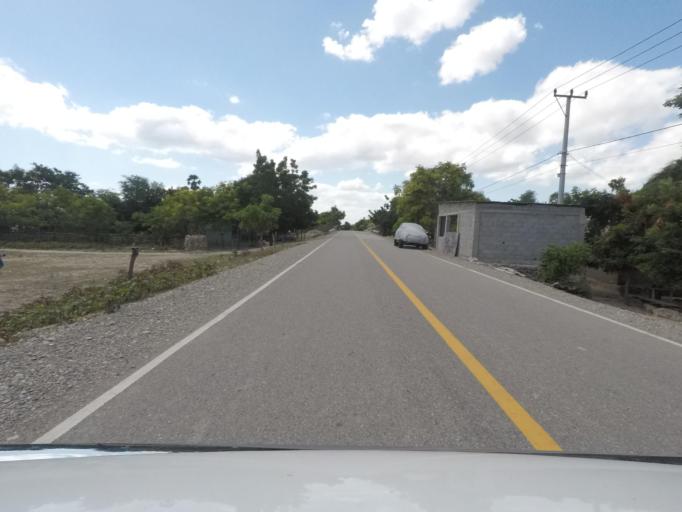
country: TL
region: Baucau
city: Baucau
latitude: -8.4310
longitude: 126.6807
